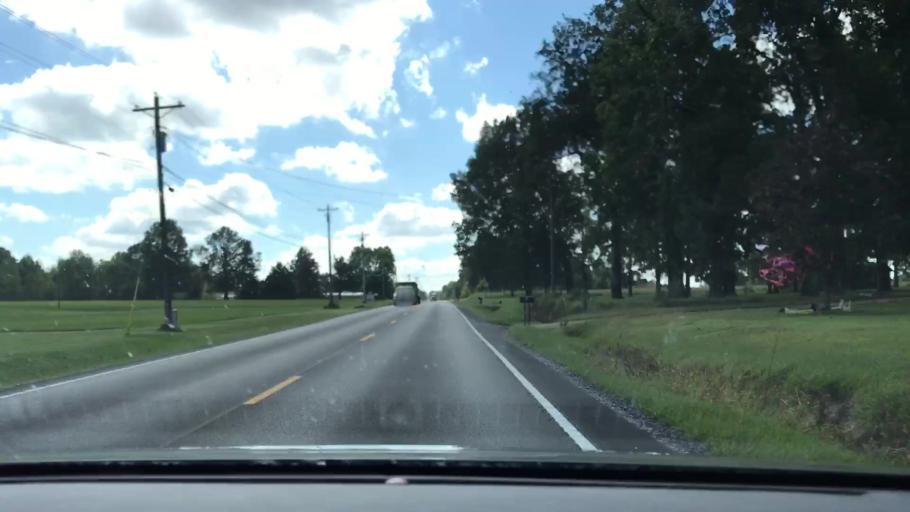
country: US
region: Kentucky
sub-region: Graves County
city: Mayfield
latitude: 36.7672
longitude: -88.5960
